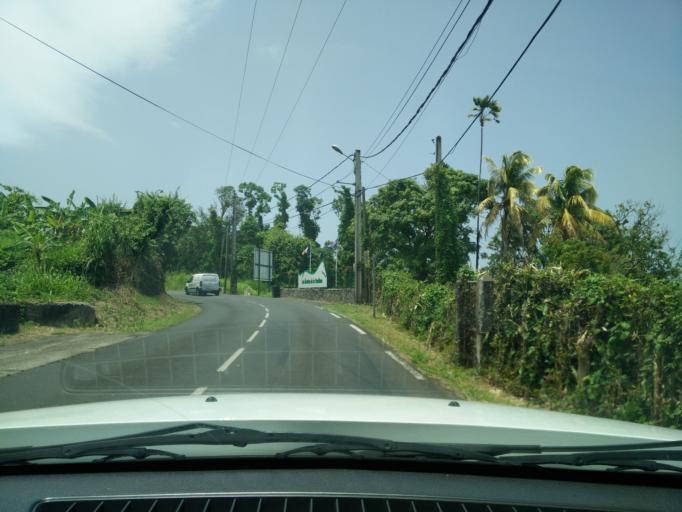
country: GP
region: Guadeloupe
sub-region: Guadeloupe
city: Trois-Rivieres
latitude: 15.9753
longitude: -61.6308
